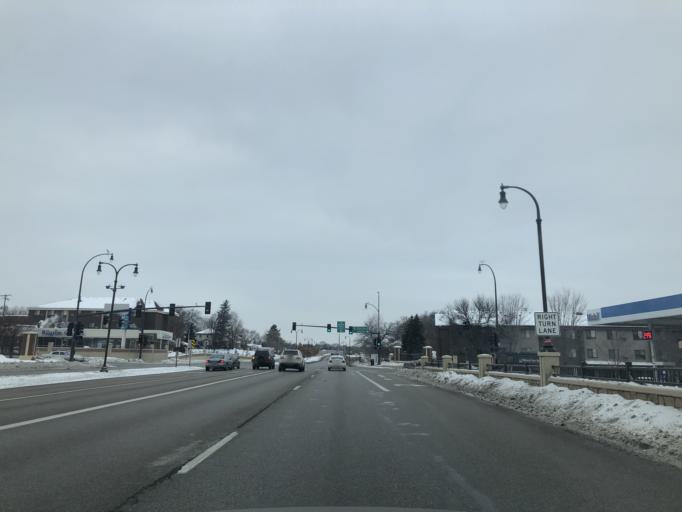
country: US
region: Minnesota
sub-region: Hennepin County
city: Robbinsdale
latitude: 45.0318
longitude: -93.3376
